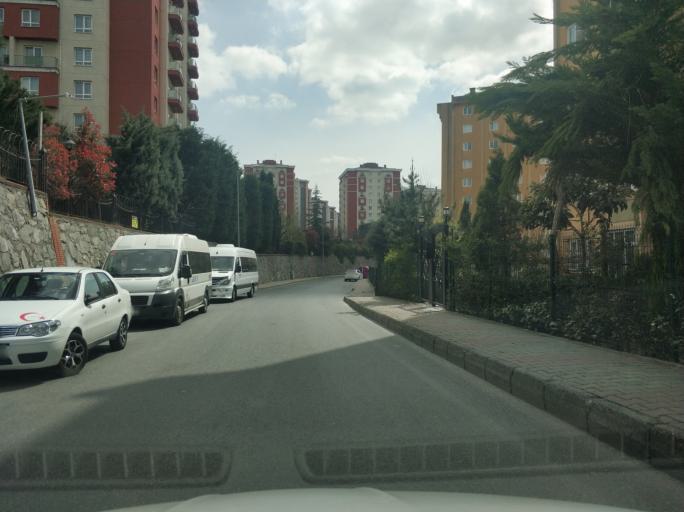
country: TR
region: Istanbul
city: Basaksehir
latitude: 41.0949
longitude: 28.8036
